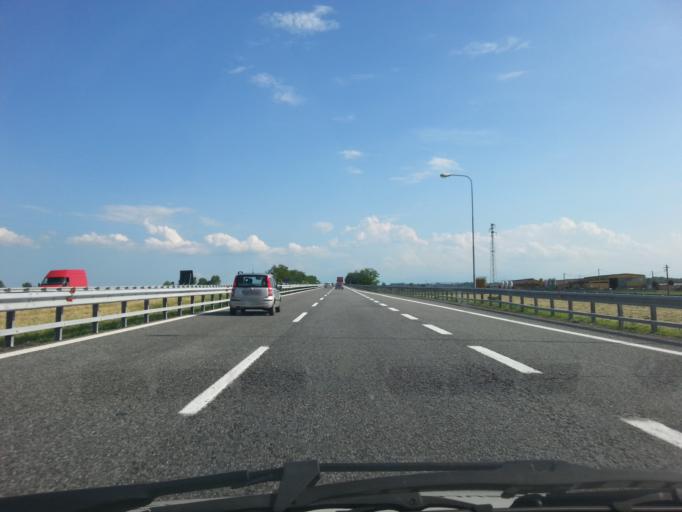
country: IT
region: Piedmont
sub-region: Provincia di Cuneo
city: Marene
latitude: 44.7021
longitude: 7.7635
